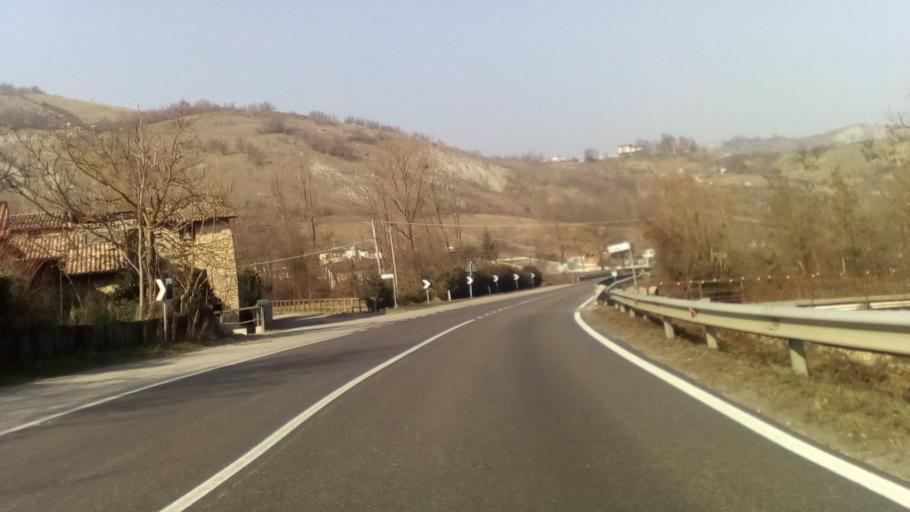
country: IT
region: Emilia-Romagna
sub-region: Provincia di Modena
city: Serramazzoni
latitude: 44.4587
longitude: 10.8323
